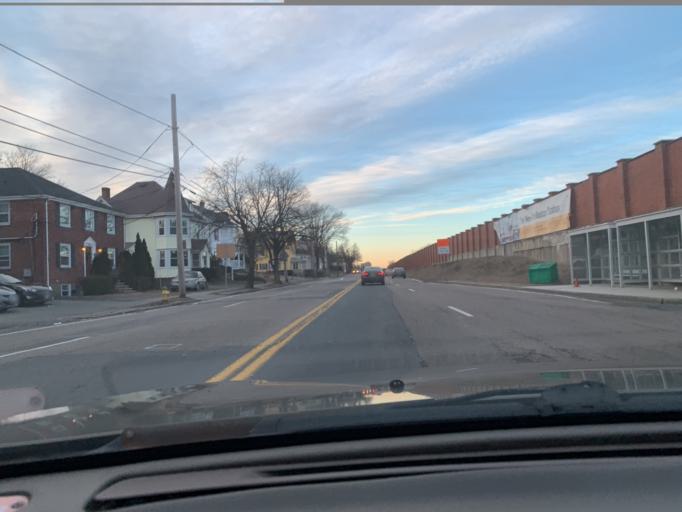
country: US
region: Massachusetts
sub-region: Norfolk County
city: Quincy
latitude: 42.2667
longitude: -71.0208
